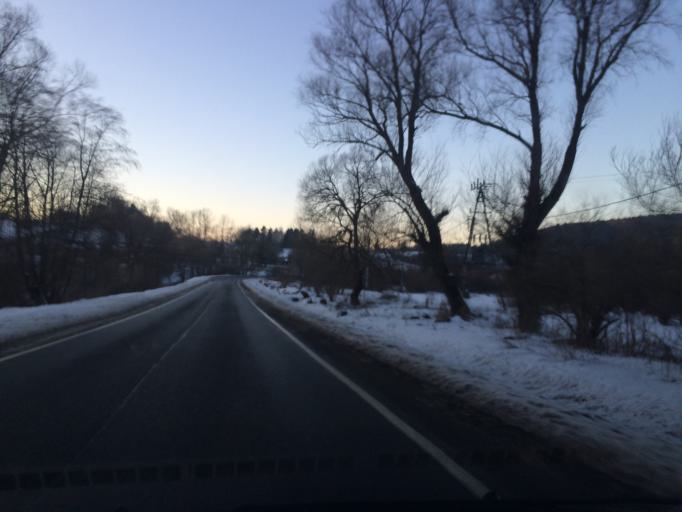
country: PL
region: Subcarpathian Voivodeship
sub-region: Powiat bieszczadzki
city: Czarna
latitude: 49.3823
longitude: 22.6393
